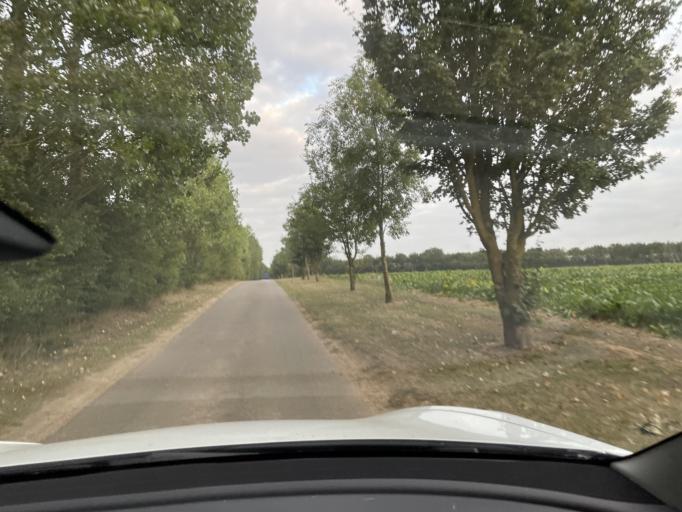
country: GB
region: England
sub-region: Cambridgeshire
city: Harston
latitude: 52.0954
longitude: 0.1066
